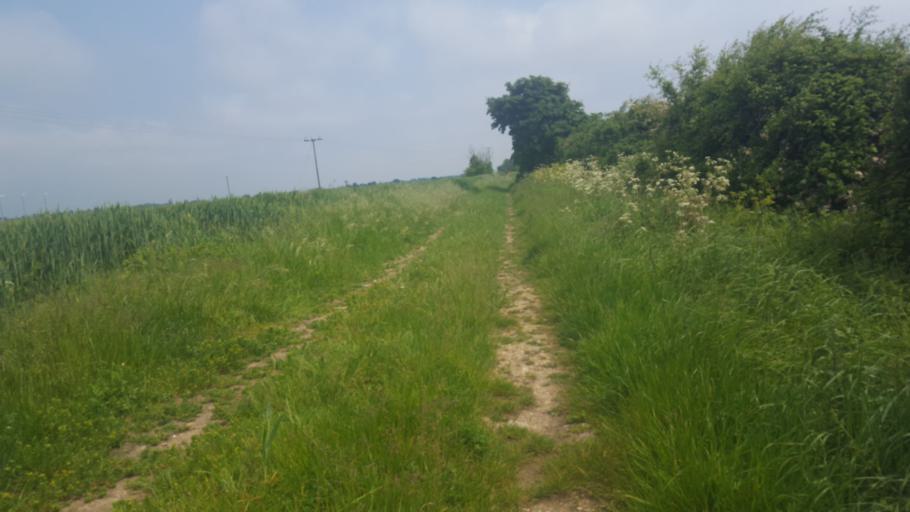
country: GB
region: England
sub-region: Essex
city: Saint Osyth
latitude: 51.7933
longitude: 1.0945
